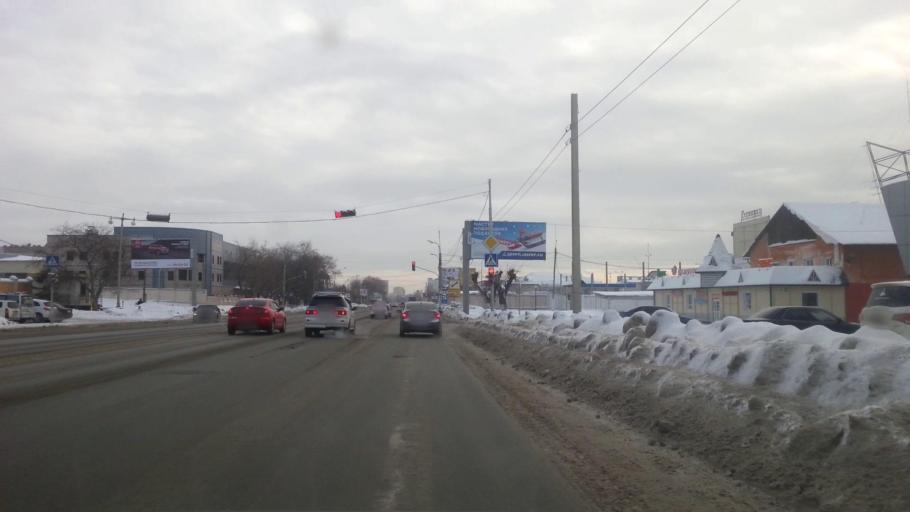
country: RU
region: Altai Krai
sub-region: Gorod Barnaulskiy
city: Barnaul
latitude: 53.3736
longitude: 83.7575
